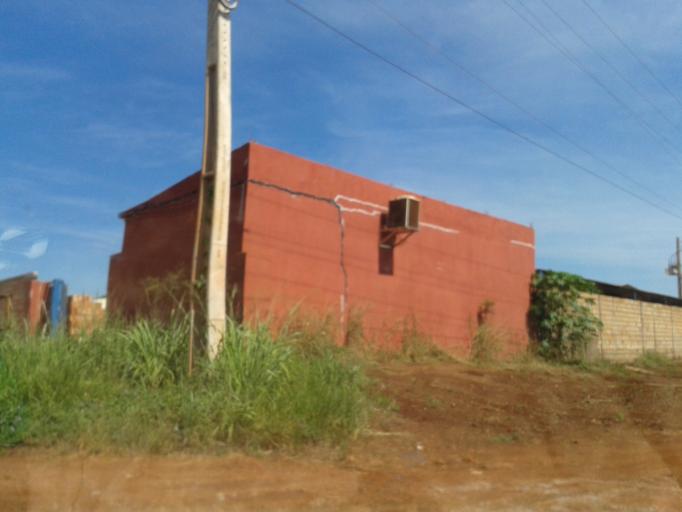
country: BR
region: Goias
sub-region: Itumbiara
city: Itumbiara
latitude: -18.4261
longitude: -49.1863
